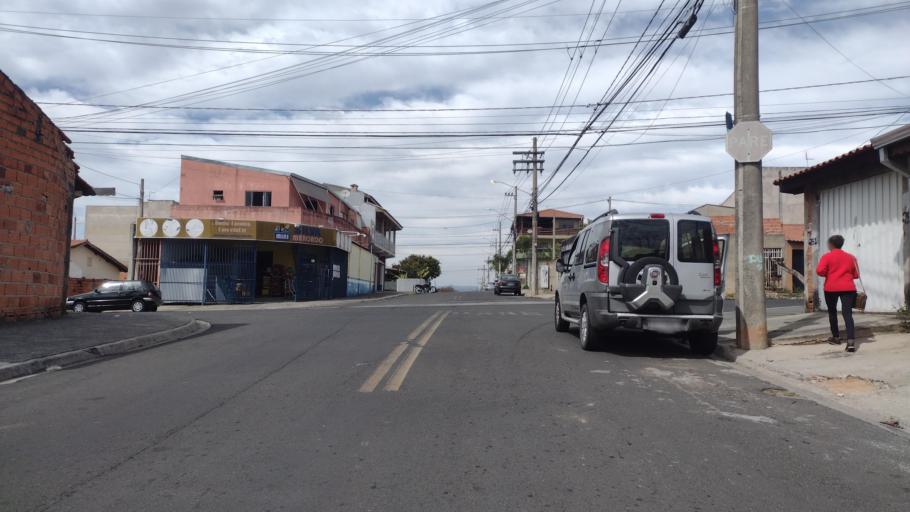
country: BR
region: Sao Paulo
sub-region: Sorocaba
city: Sorocaba
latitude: -23.4260
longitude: -47.4593
